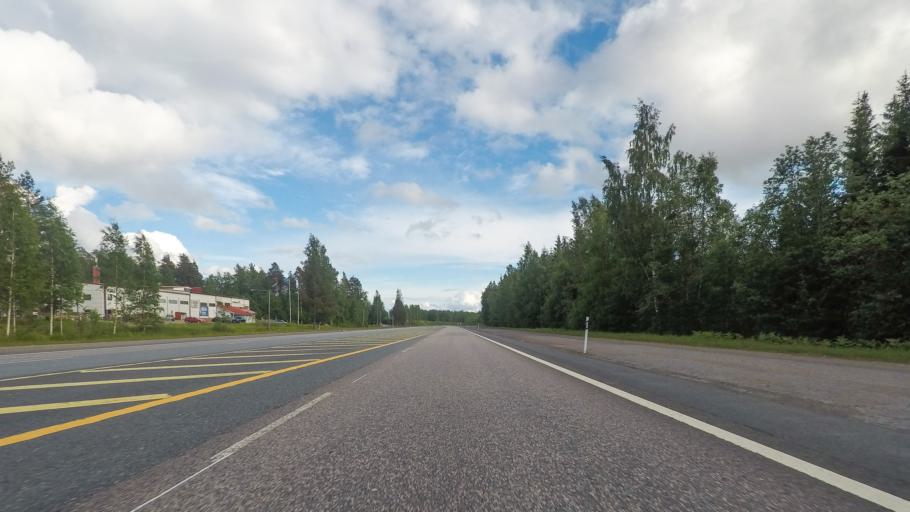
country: FI
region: Central Finland
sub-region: Joutsa
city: Joutsa
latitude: 61.7617
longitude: 26.1057
